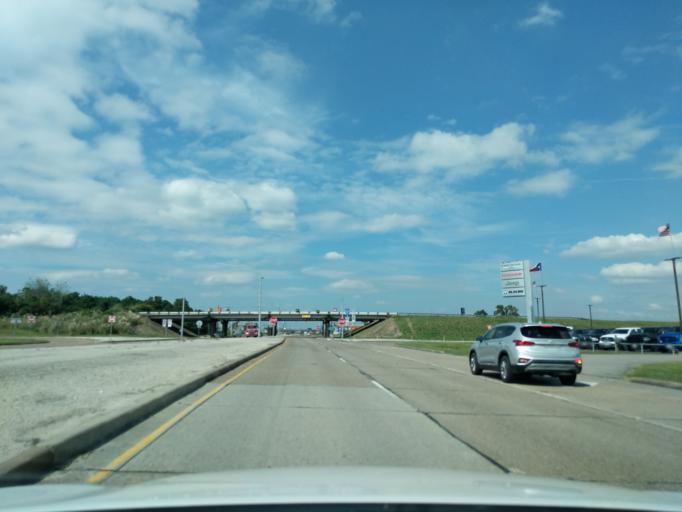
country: US
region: Texas
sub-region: Chambers County
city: Winnie
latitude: 29.8254
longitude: -94.3840
